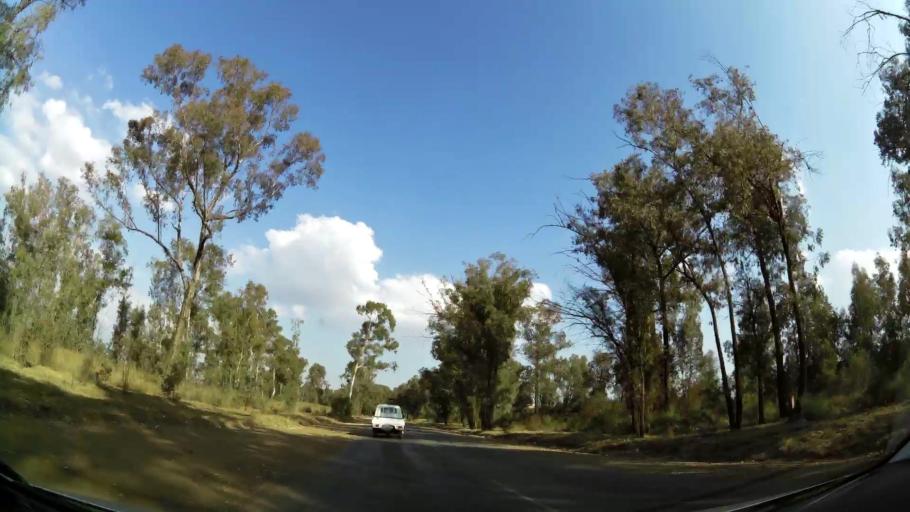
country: ZA
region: Gauteng
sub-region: Ekurhuleni Metropolitan Municipality
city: Tembisa
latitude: -25.9355
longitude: 28.2327
